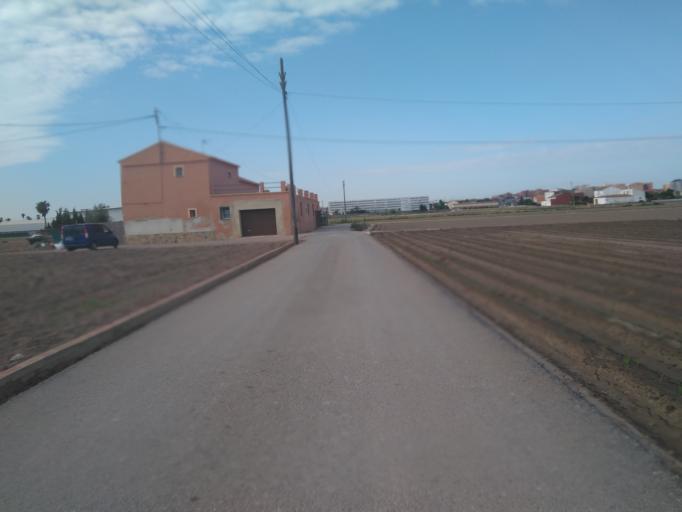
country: ES
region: Valencia
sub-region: Provincia de Valencia
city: Alboraya
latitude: 39.4921
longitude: -0.3403
